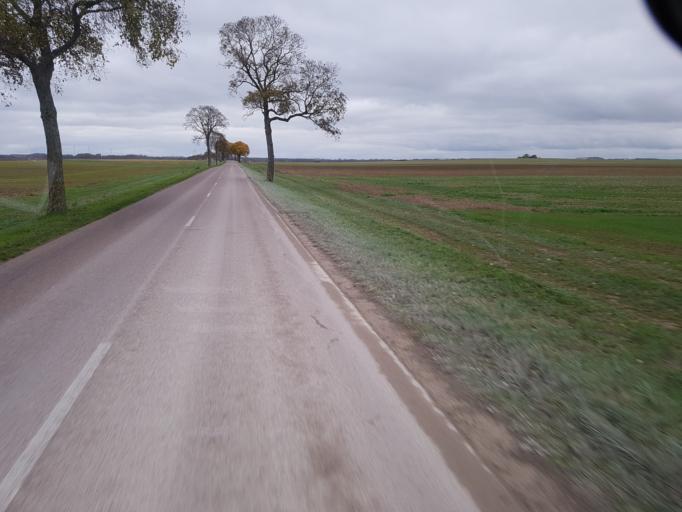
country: FR
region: Champagne-Ardenne
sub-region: Departement de l'Aube
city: Mery-sur-Seine
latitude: 48.5336
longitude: 3.8679
